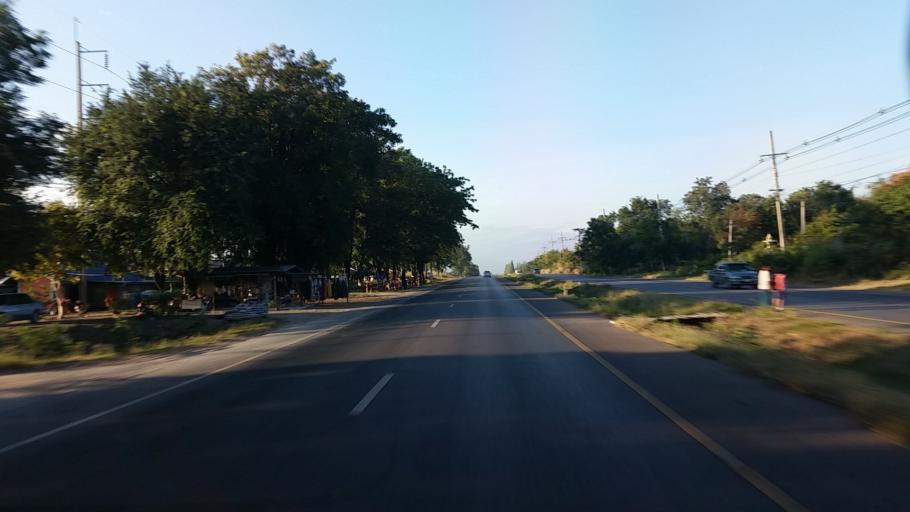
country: TH
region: Lop Buri
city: Chai Badan
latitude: 15.1970
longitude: 101.0835
